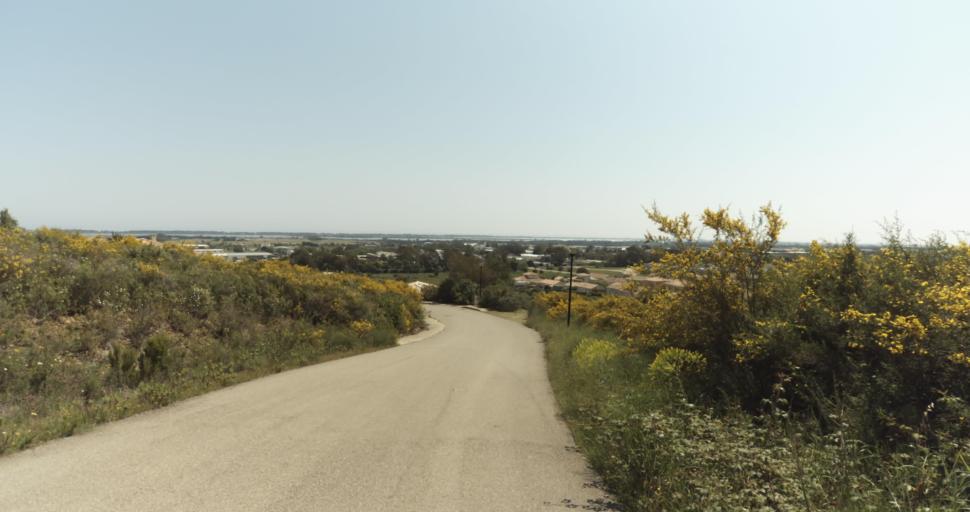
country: FR
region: Corsica
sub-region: Departement de la Haute-Corse
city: Biguglia
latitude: 42.6023
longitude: 9.4297
